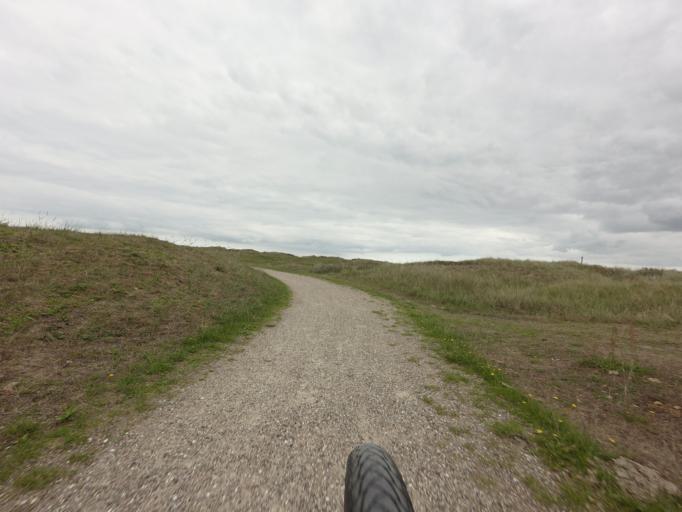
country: DK
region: North Denmark
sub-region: Hjorring Kommune
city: Sindal
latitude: 57.5881
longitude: 10.1477
